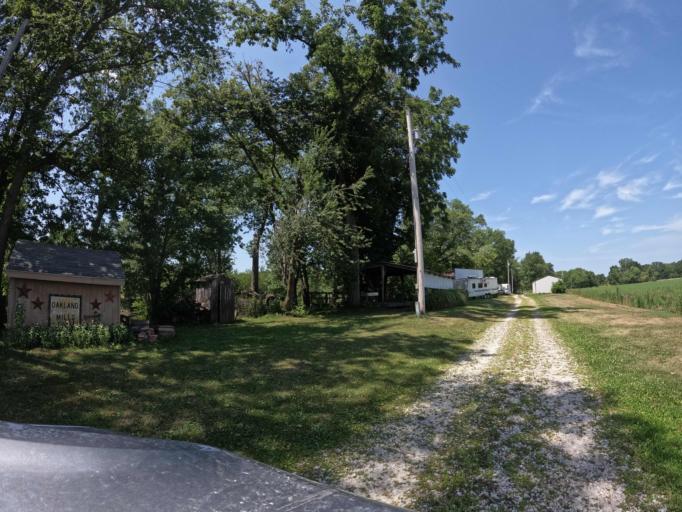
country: US
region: Iowa
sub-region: Henry County
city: Mount Pleasant
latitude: 40.8991
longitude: -91.5569
